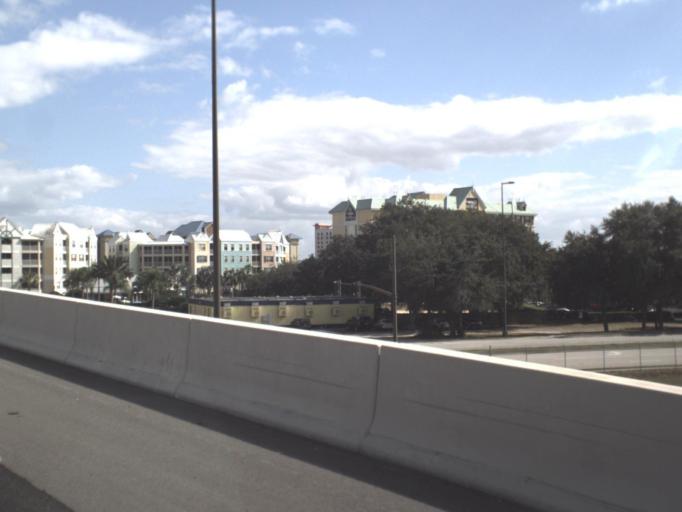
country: US
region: Florida
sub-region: Osceola County
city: Celebration
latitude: 28.3401
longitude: -81.4860
